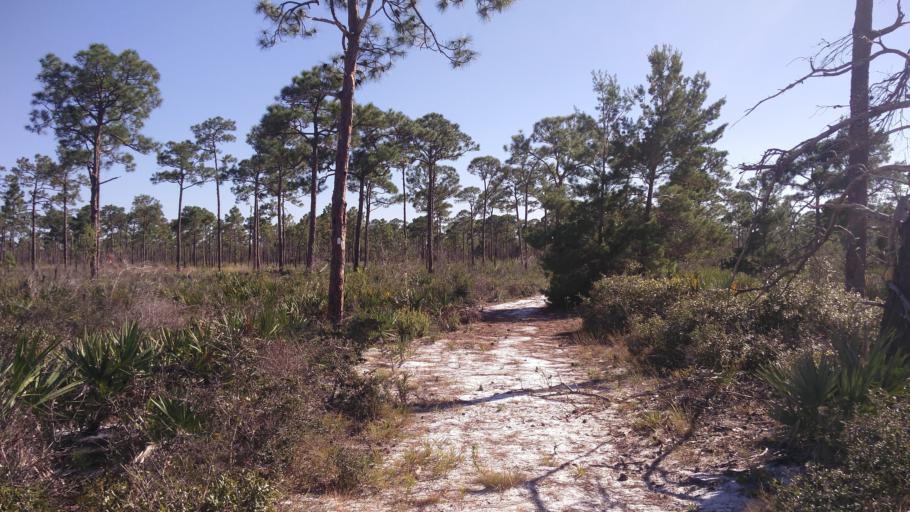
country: US
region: Florida
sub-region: Palm Beach County
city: Tequesta
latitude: 27.0118
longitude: -80.1245
